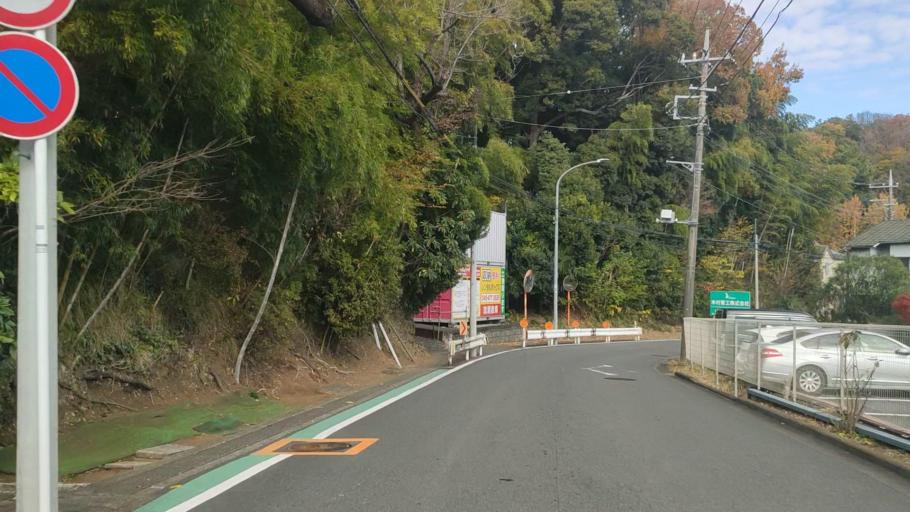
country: JP
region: Kanagawa
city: Yokohama
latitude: 35.4446
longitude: 139.5563
